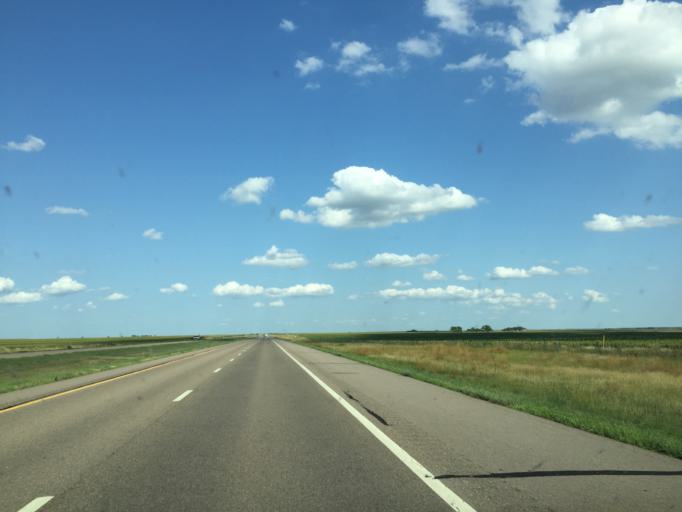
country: US
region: Kansas
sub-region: Trego County
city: WaKeeney
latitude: 39.0232
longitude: -100.0727
